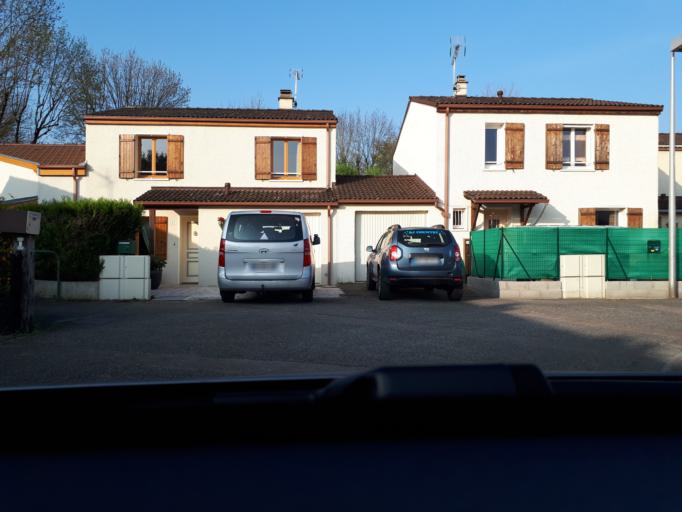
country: FR
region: Rhone-Alpes
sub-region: Departement de l'Isere
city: Bourgoin-Jallieu
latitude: 45.6110
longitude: 5.2681
